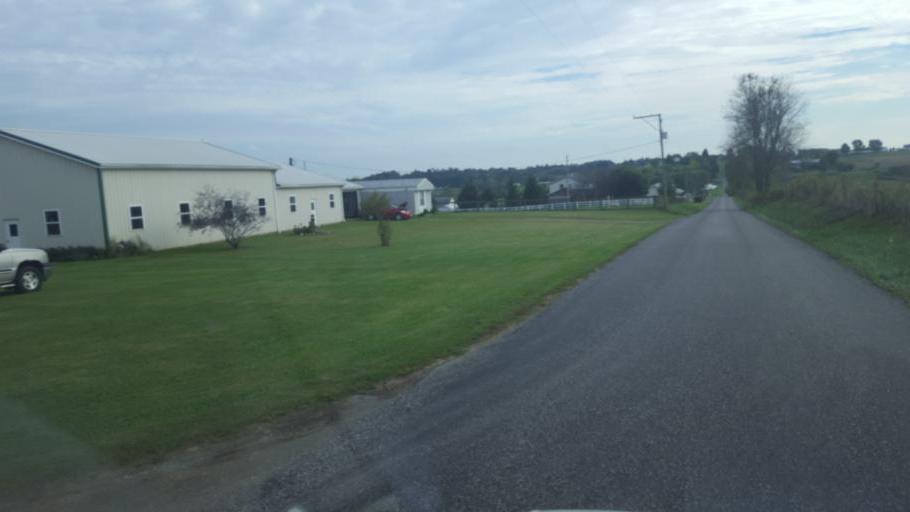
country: US
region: Ohio
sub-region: Holmes County
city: Millersburg
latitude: 40.5643
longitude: -81.8400
